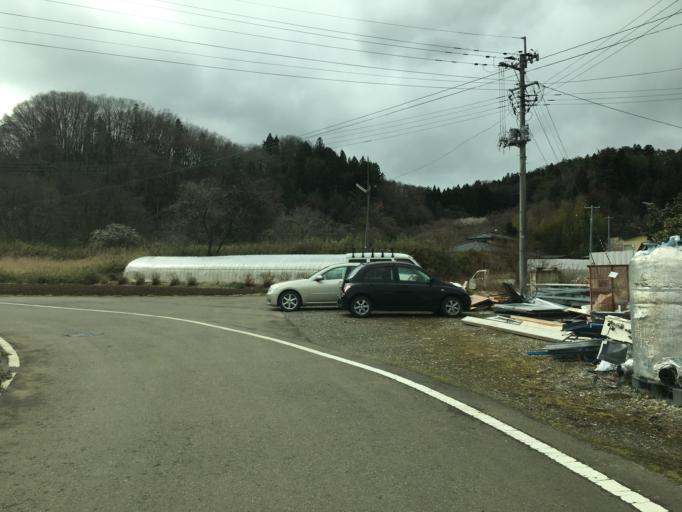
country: JP
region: Fukushima
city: Fukushima-shi
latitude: 37.7114
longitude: 140.4264
